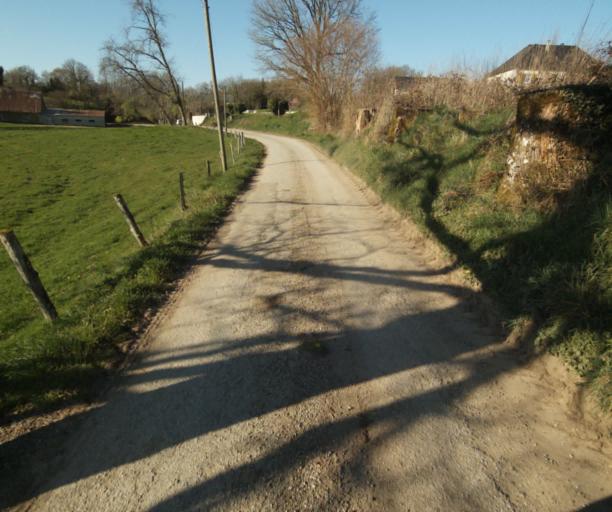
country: FR
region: Limousin
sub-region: Departement de la Correze
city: Chamboulive
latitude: 45.4964
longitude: 1.7288
